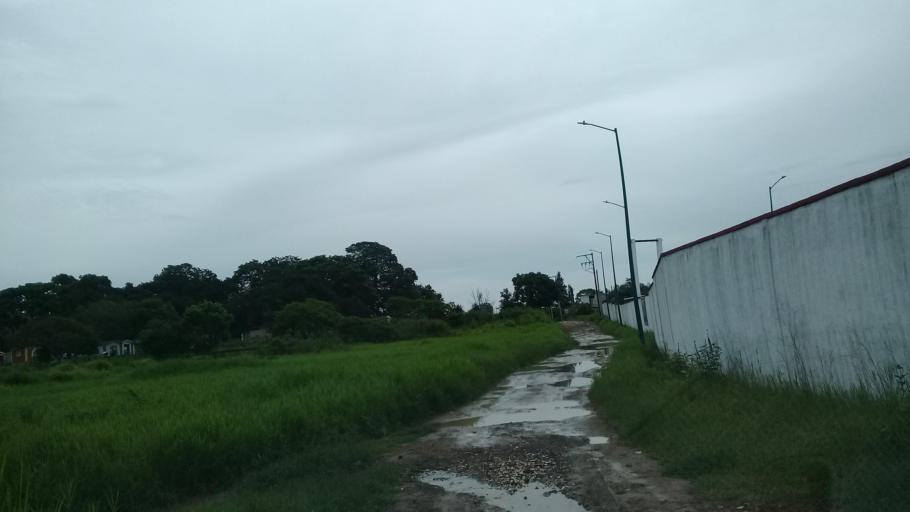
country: MX
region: Veracruz
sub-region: Emiliano Zapata
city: Dos Rios
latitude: 19.4806
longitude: -96.8017
